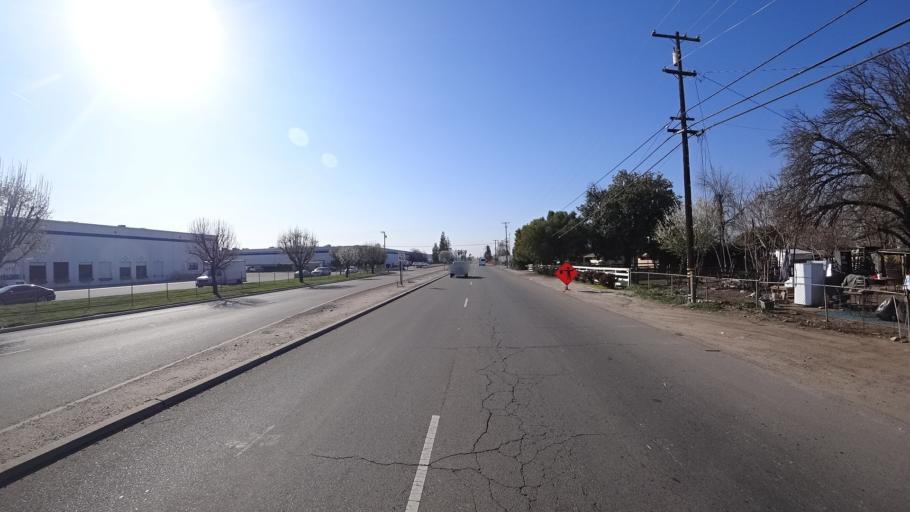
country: US
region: California
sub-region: Fresno County
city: Fresno
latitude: 36.6915
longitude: -119.7366
